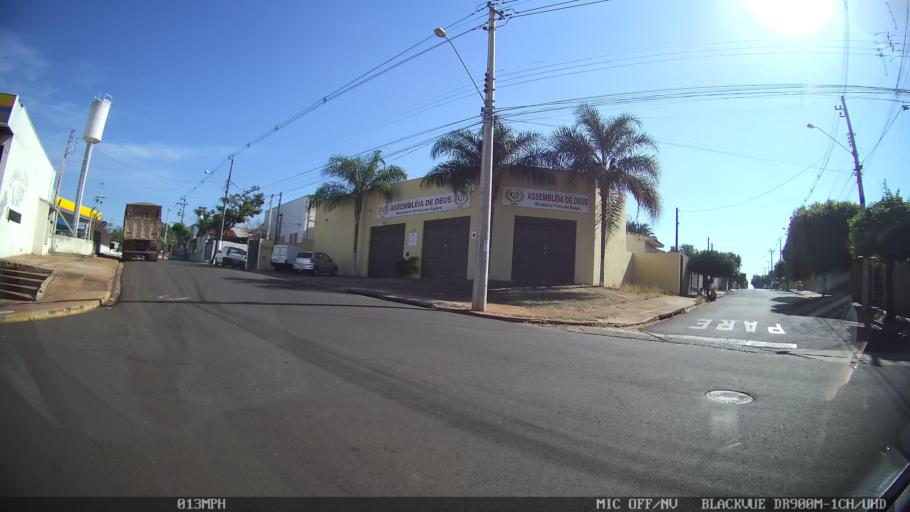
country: BR
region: Sao Paulo
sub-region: Sao Jose Do Rio Preto
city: Sao Jose do Rio Preto
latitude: -20.7871
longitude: -49.3895
